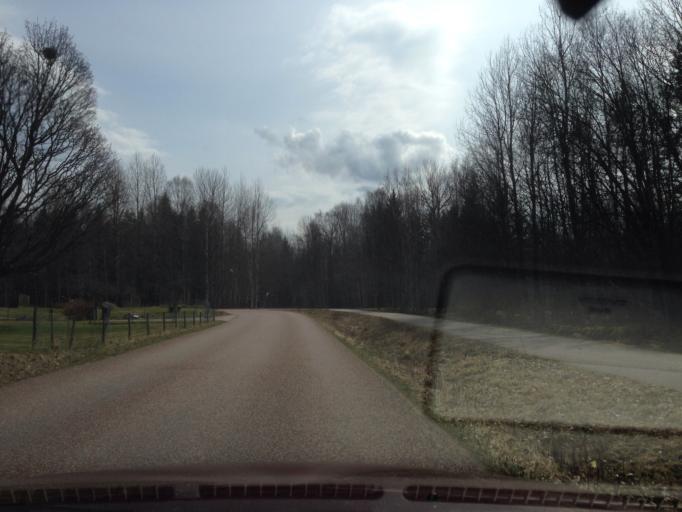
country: SE
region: Dalarna
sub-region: Ludvika Kommun
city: Grangesberg
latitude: 60.1239
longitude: 15.0547
